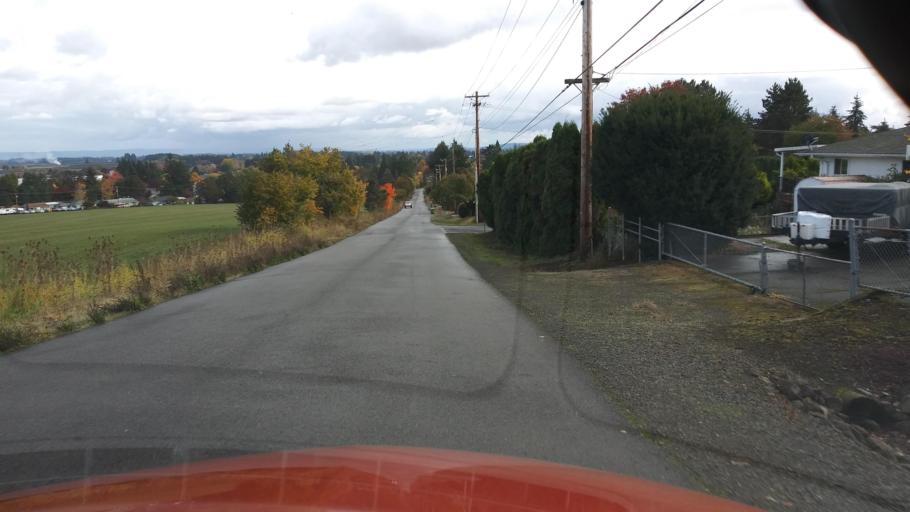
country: US
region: Oregon
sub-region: Washington County
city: Forest Grove
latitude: 45.5333
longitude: -123.1356
